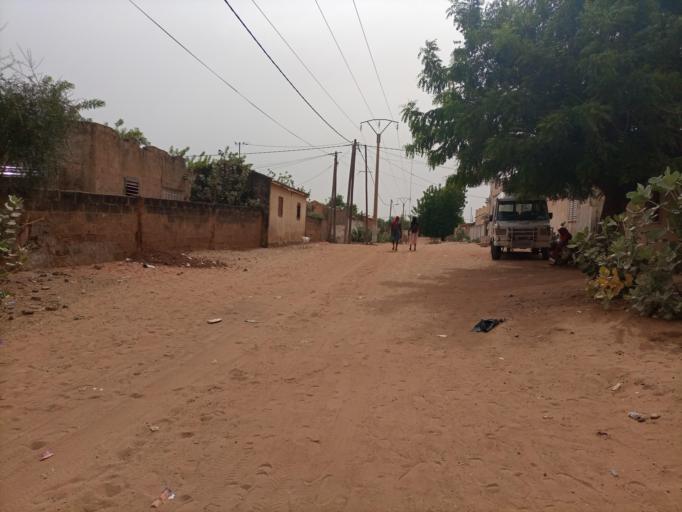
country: SN
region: Louga
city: Ndibene Dahra
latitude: 15.3974
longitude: -15.1172
